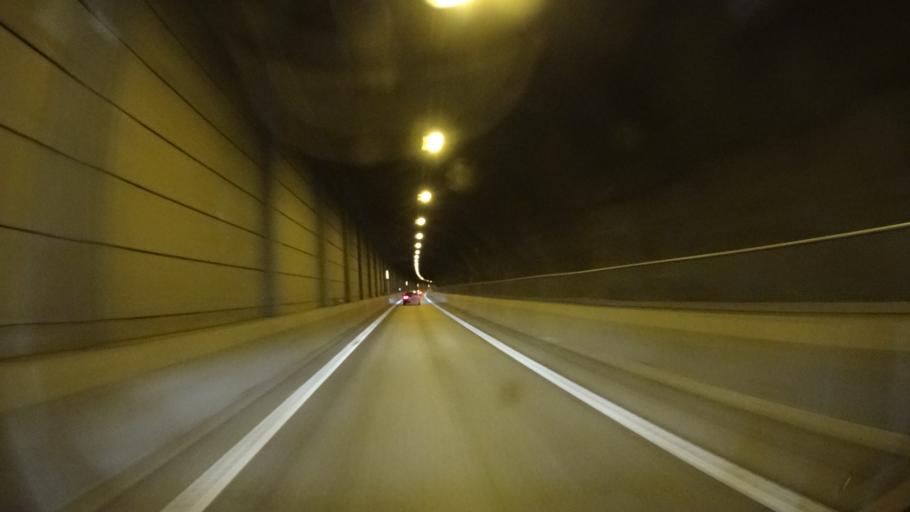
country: SE
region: Stockholm
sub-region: Taby Kommun
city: Taby
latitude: 59.4857
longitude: 18.1020
